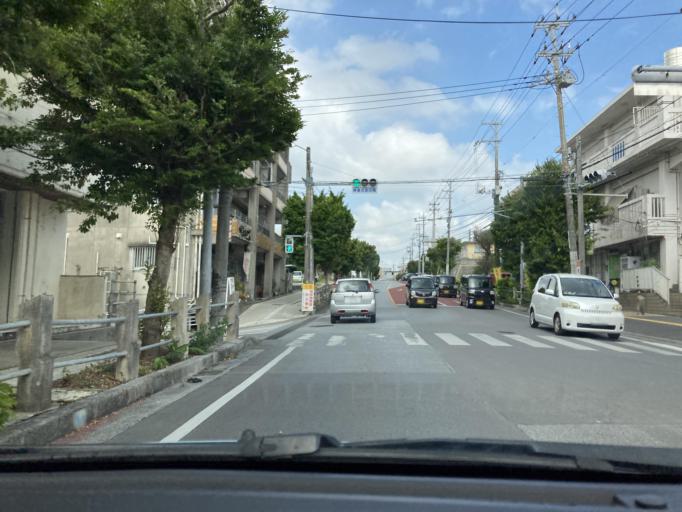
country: JP
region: Okinawa
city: Ginowan
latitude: 26.2237
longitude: 127.7337
